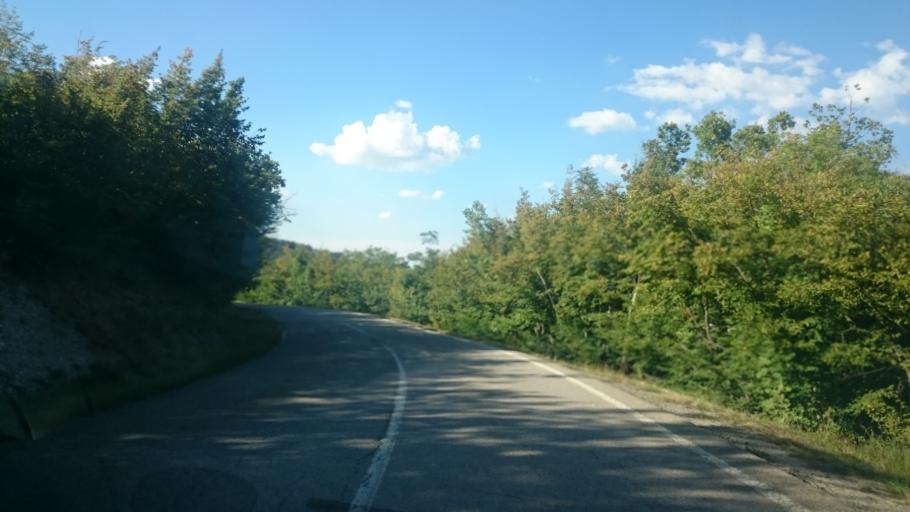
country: IT
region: Emilia-Romagna
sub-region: Provincia di Reggio Emilia
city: Villa Minozzo
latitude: 44.3472
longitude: 10.4595
